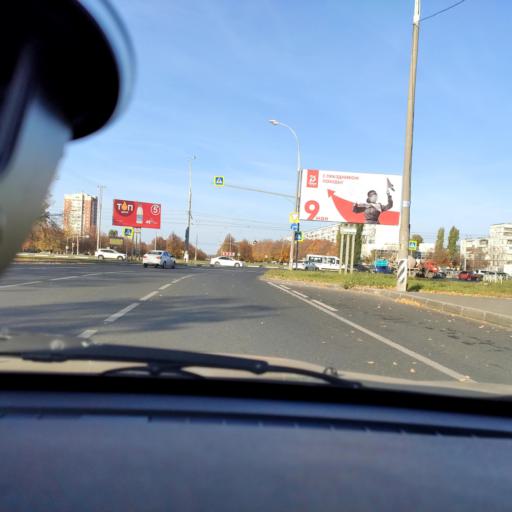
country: RU
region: Samara
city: Tol'yatti
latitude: 53.5185
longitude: 49.2967
